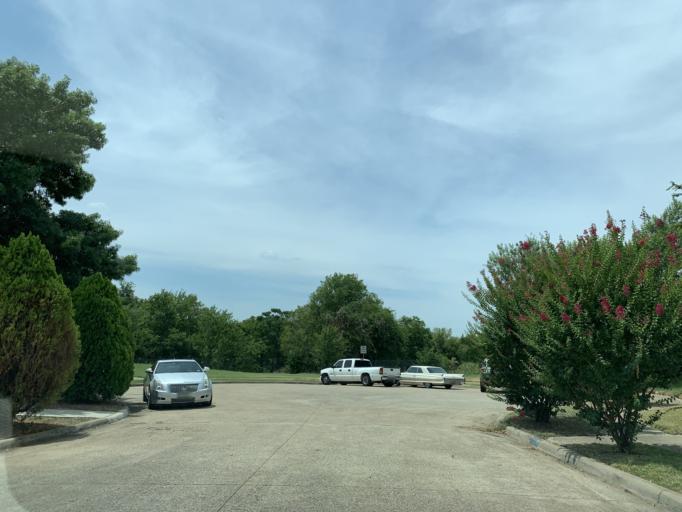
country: US
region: Texas
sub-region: Dallas County
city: Grand Prairie
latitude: 32.6606
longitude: -97.0331
